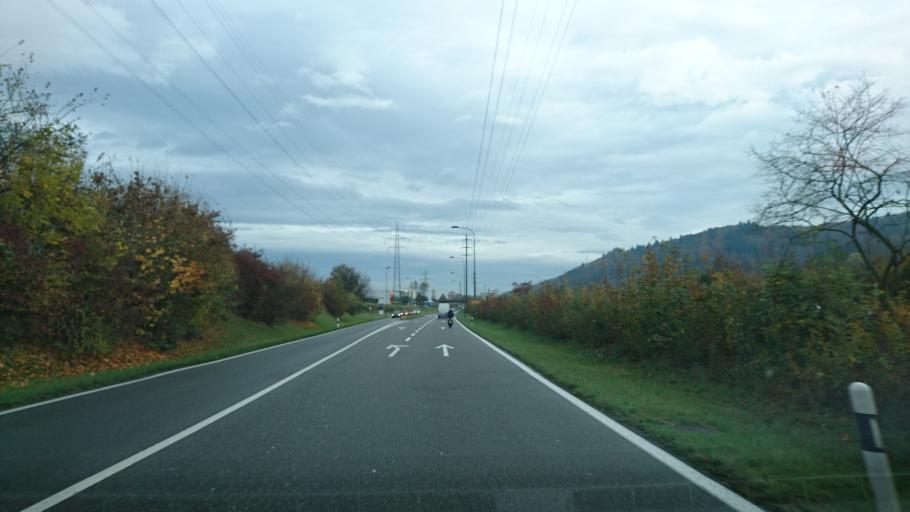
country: CH
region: Aargau
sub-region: Bezirk Aarau
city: Oberentfelden
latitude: 47.3480
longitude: 8.0505
